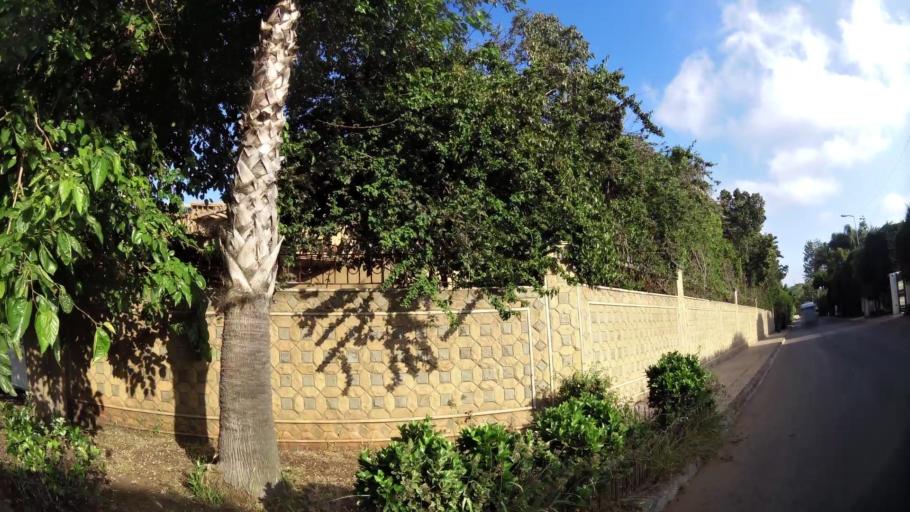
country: MA
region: Rabat-Sale-Zemmour-Zaer
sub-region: Rabat
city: Rabat
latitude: 33.9596
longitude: -6.8494
